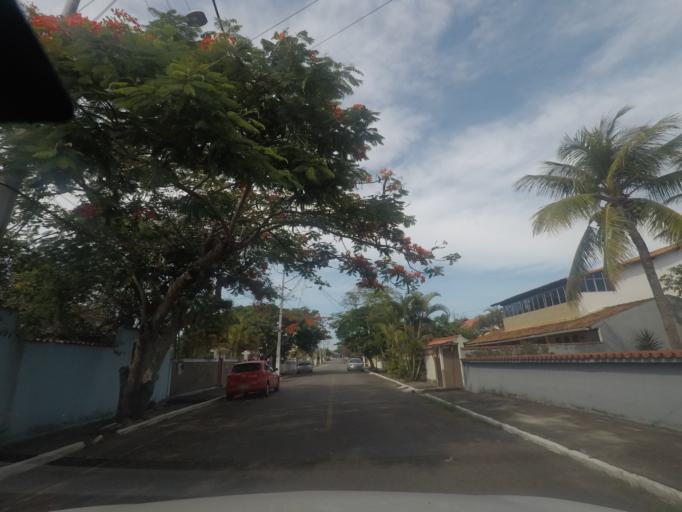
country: BR
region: Rio de Janeiro
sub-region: Marica
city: Marica
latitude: -22.9563
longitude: -42.8125
